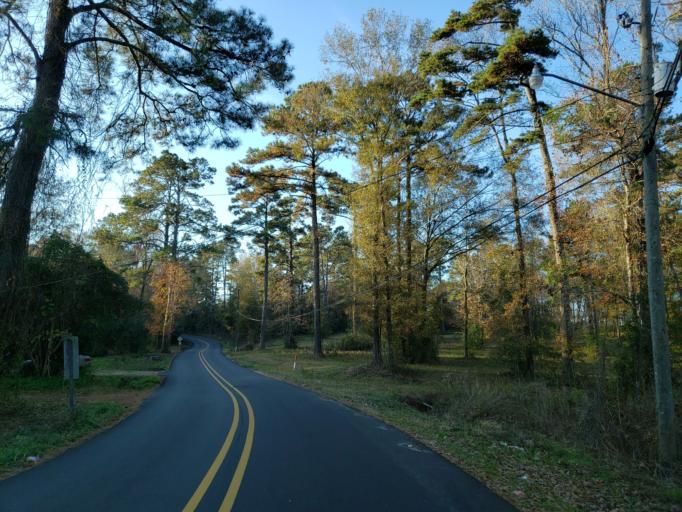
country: US
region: Mississippi
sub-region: Lamar County
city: Arnold Line
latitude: 31.3500
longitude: -89.3536
